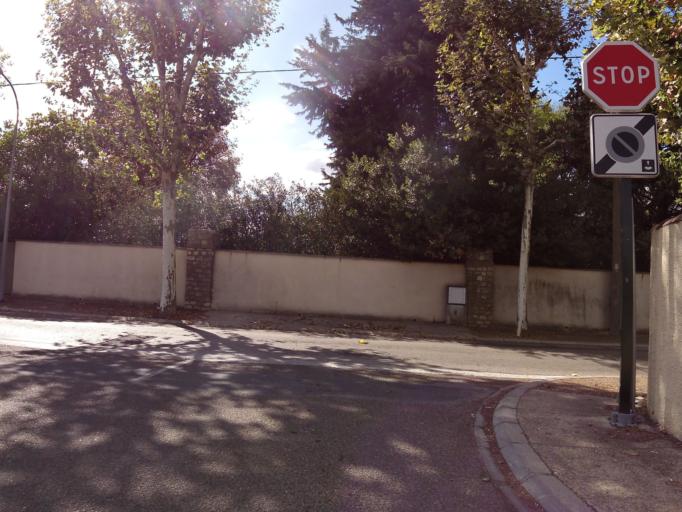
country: FR
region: Languedoc-Roussillon
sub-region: Departement du Gard
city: Vergeze
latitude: 43.7379
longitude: 4.2196
